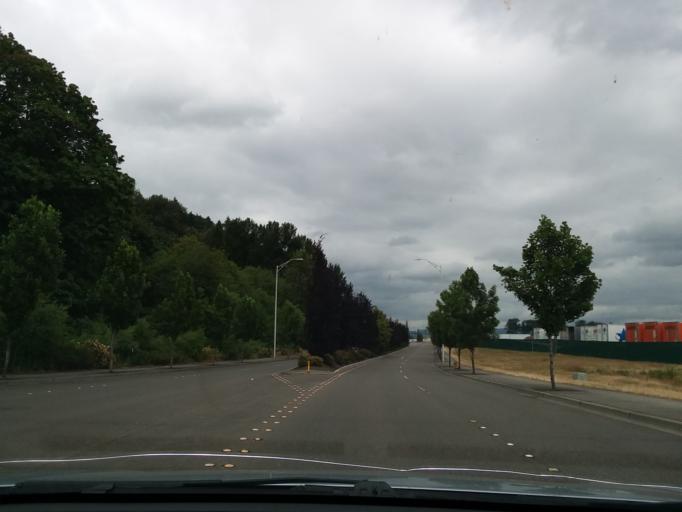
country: US
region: Washington
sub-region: King County
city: SeaTac
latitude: 47.4270
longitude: -122.2700
